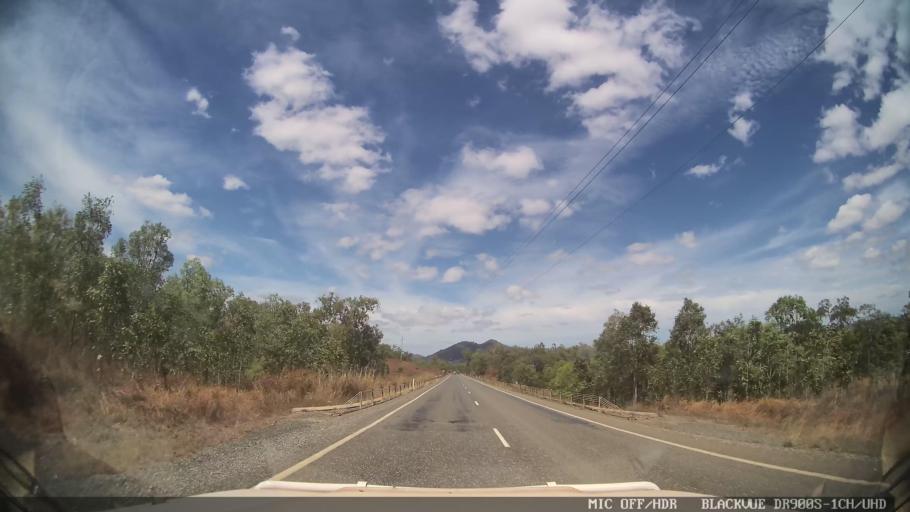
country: AU
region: Queensland
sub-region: Cook
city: Cooktown
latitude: -15.6096
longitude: 145.2215
